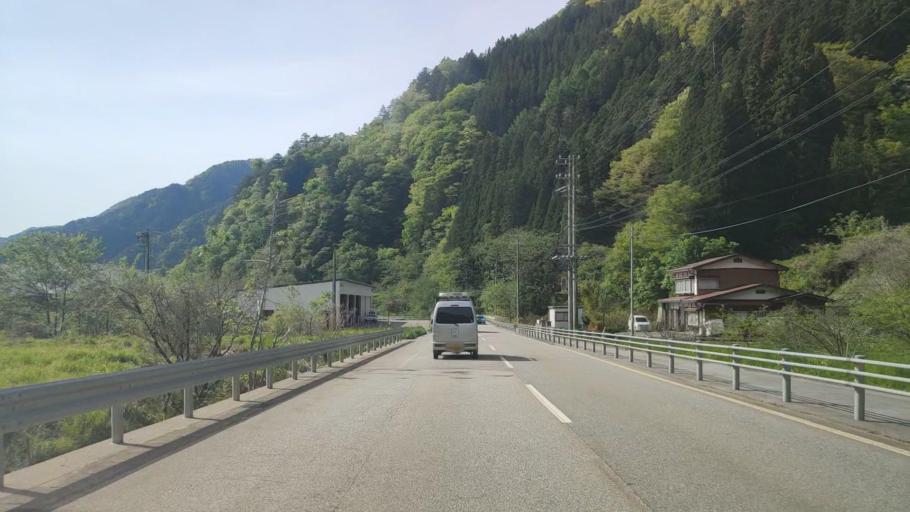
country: JP
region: Gifu
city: Takayama
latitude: 36.2534
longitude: 137.4773
